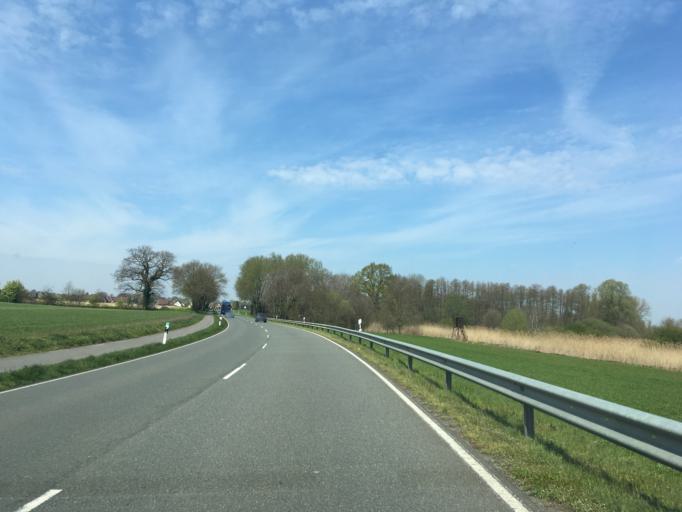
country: DE
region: North Rhine-Westphalia
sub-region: Regierungsbezirk Munster
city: Vreden
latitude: 52.0199
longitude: 6.8426
